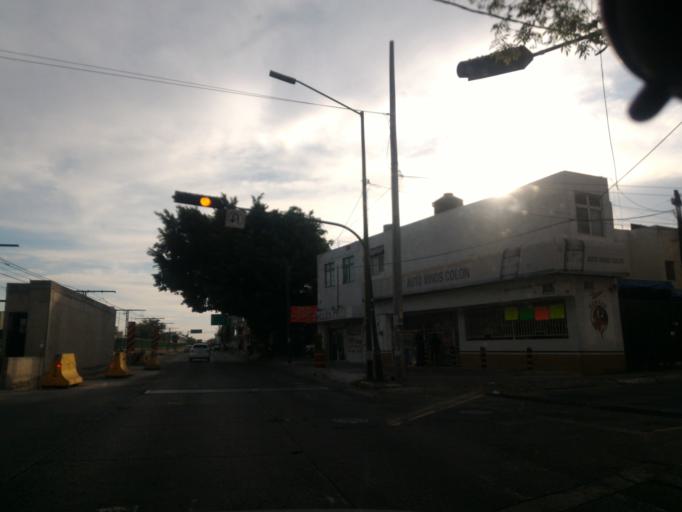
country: MX
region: Jalisco
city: Guadalajara
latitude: 20.6541
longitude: -103.3640
